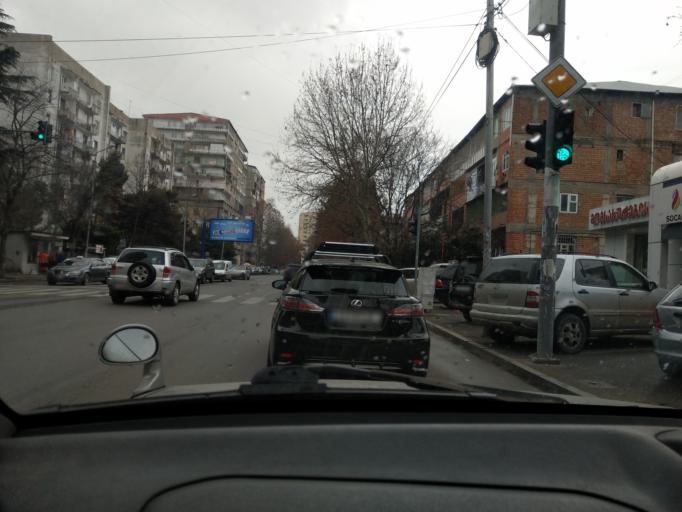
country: GE
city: Tsqnet'i
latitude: 41.7215
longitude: 44.7645
